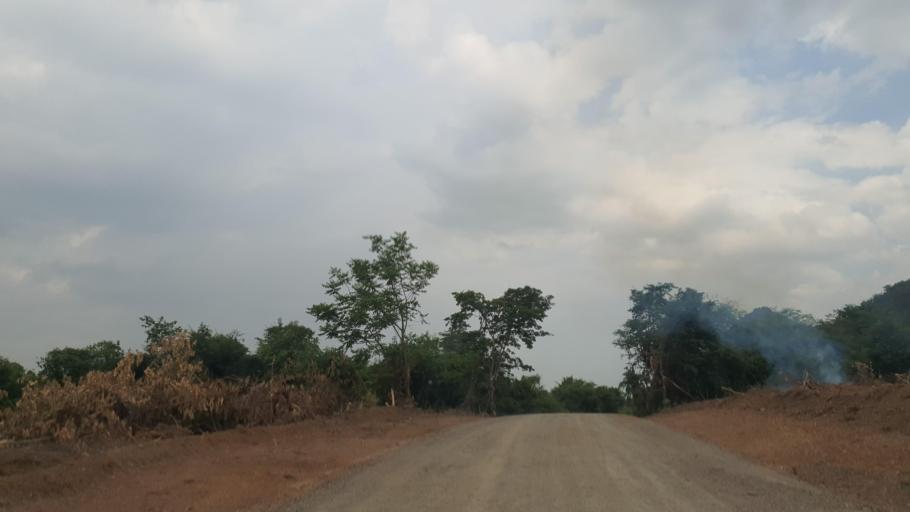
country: TH
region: Sukhothai
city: Thung Saliam
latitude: 17.2653
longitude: 99.5380
